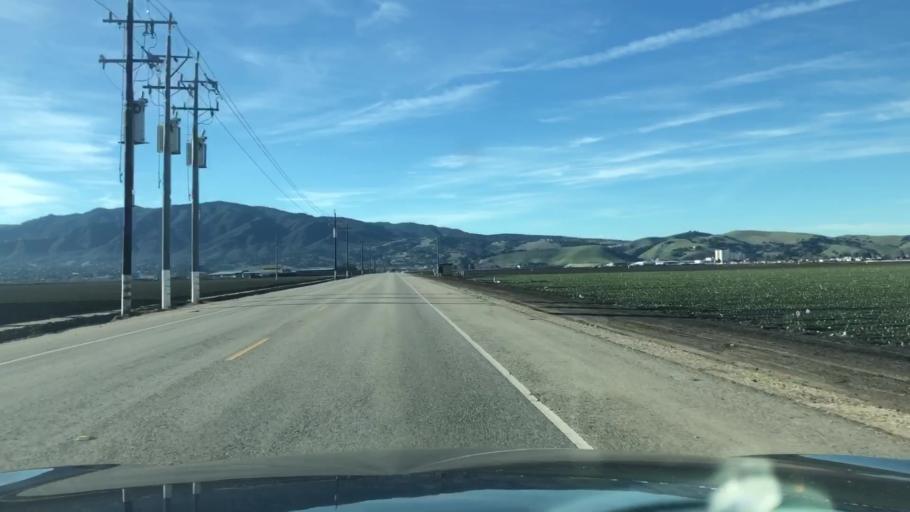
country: US
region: California
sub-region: Monterey County
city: Salinas
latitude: 36.6345
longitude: -121.6213
